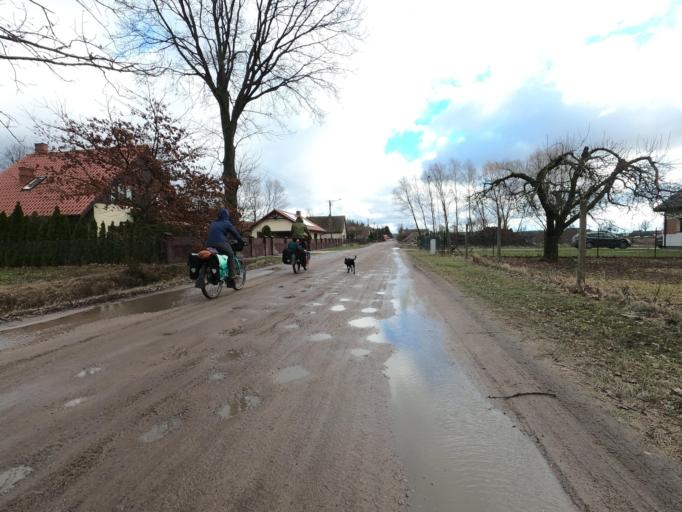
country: PL
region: Greater Poland Voivodeship
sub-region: Powiat pilski
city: Miasteczko Krajenskie
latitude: 53.1118
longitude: 17.0048
